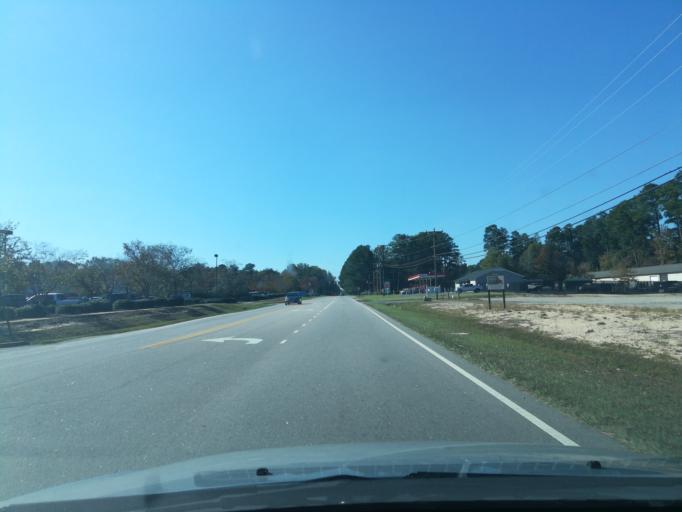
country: US
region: North Carolina
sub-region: Durham County
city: Durham
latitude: 36.0330
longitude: -78.9791
